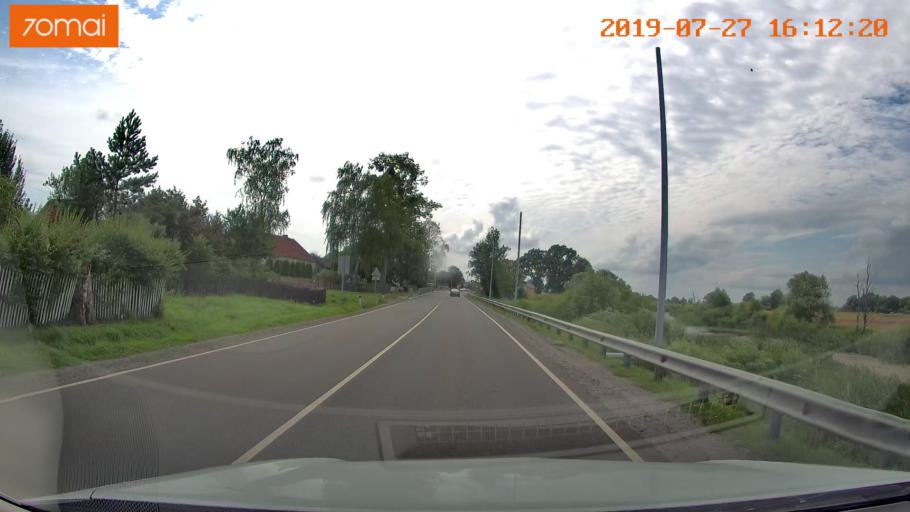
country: RU
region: Kaliningrad
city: Chernyakhovsk
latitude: 54.6310
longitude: 21.6568
